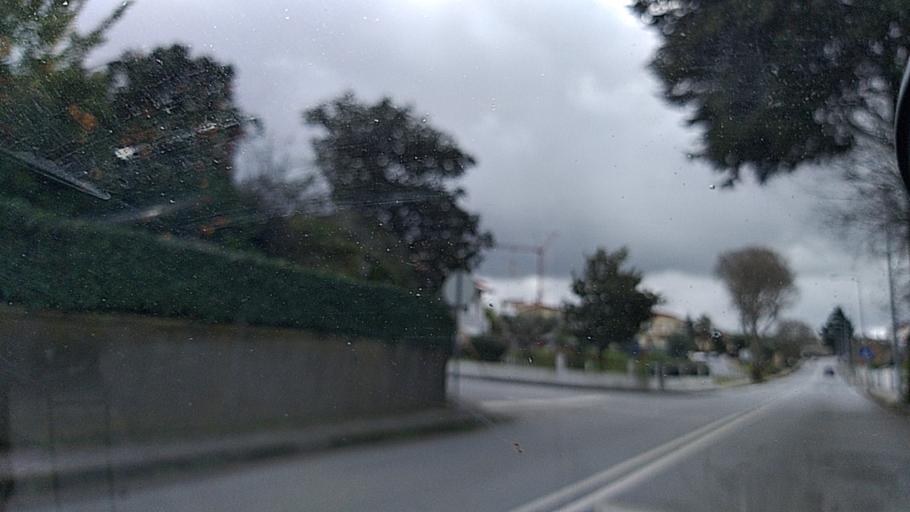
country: PT
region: Viseu
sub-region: Mangualde
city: Mangualde
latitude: 40.6143
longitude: -7.7597
